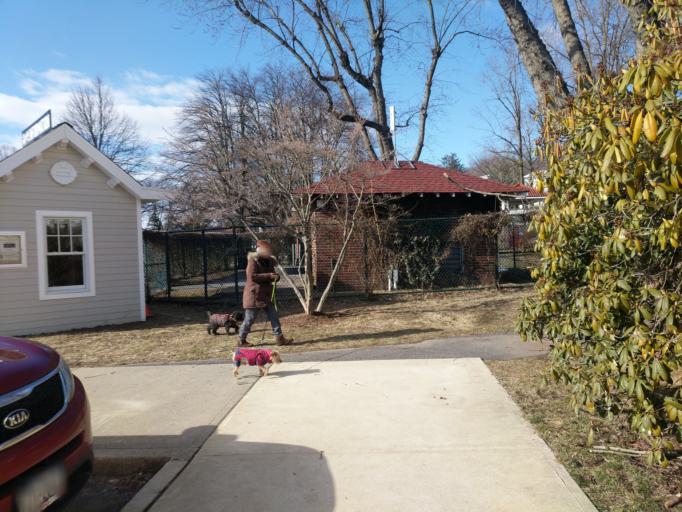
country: US
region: New York
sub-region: Suffolk County
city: Northport
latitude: 40.9005
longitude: -73.3520
